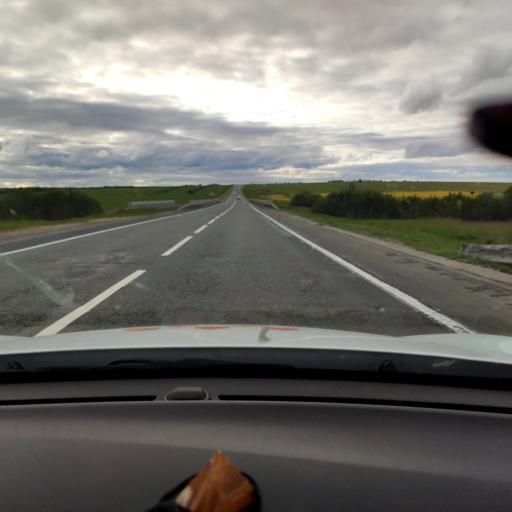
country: RU
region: Tatarstan
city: Laishevo
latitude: 55.5182
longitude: 49.8028
